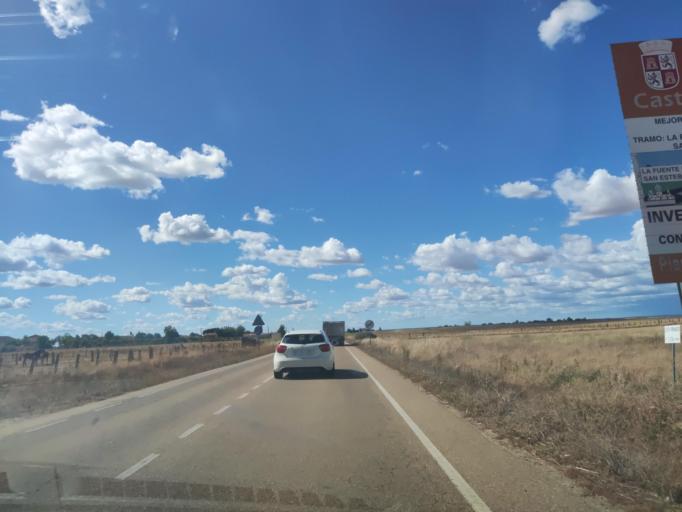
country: ES
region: Castille and Leon
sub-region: Provincia de Salamanca
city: La Fuente de San Esteban
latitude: 40.7955
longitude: -6.2475
